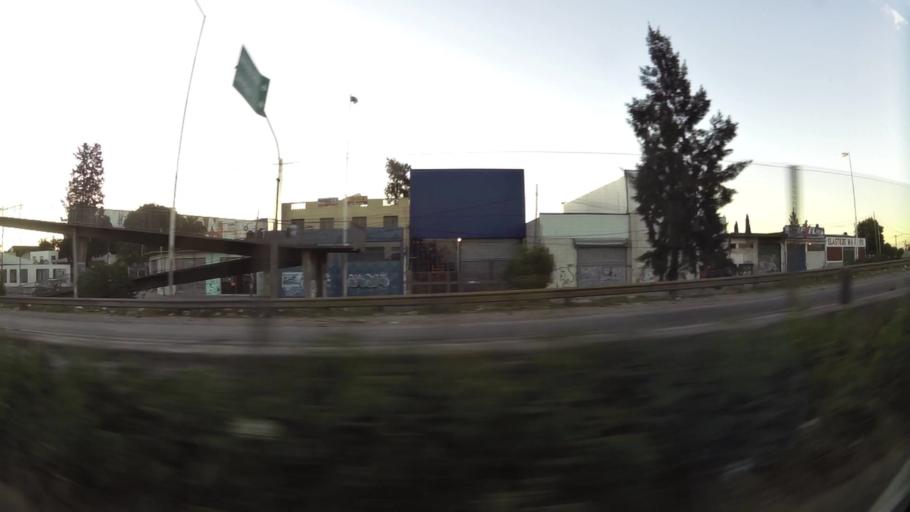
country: AR
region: Buenos Aires
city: Pontevedra
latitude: -34.7632
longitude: -58.6170
